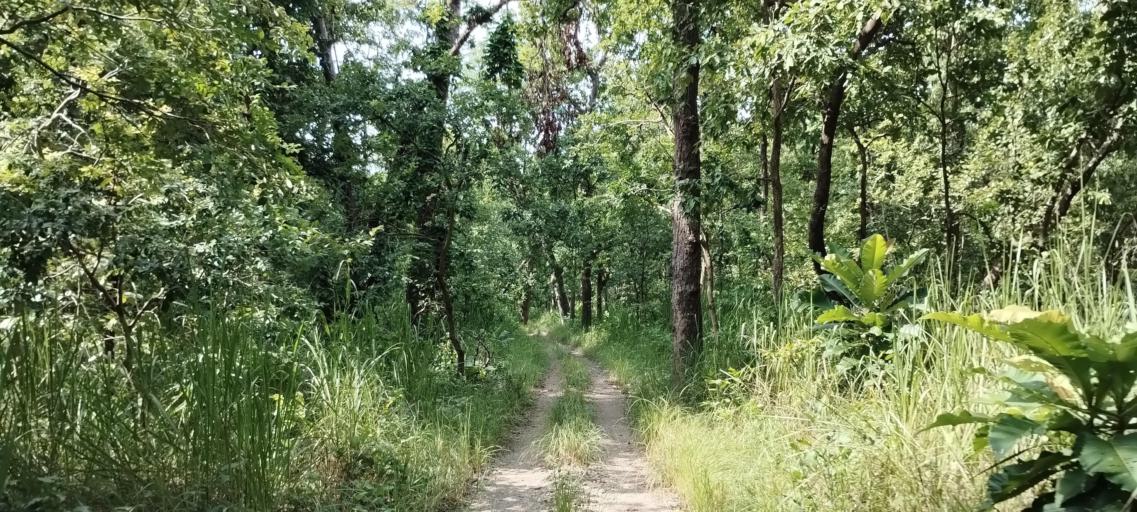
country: NP
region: Far Western
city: Tikapur
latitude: 28.5633
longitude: 81.2941
